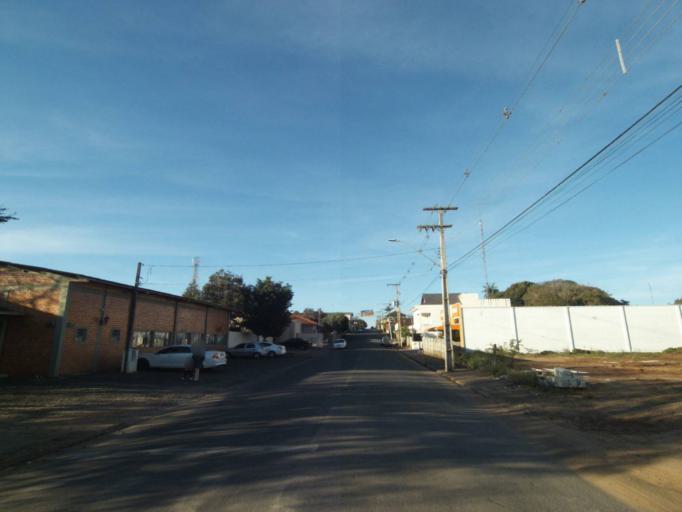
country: BR
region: Parana
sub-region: Tibagi
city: Tibagi
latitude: -24.5179
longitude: -50.4102
